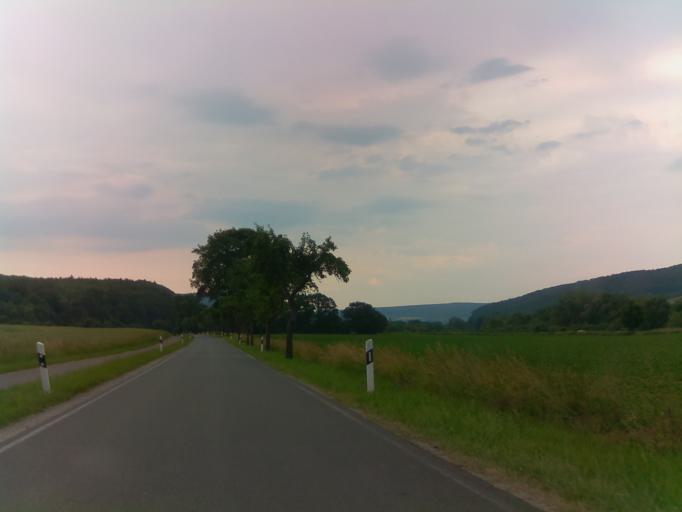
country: DE
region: Lower Saxony
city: Polle
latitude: 51.8937
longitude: 9.4124
